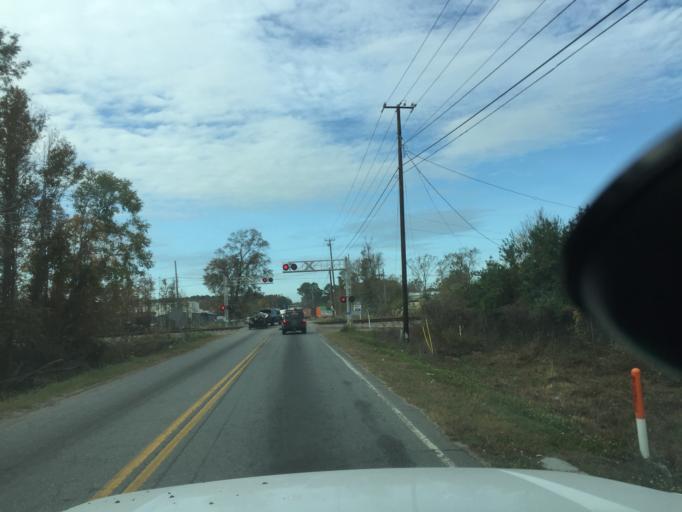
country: US
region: Georgia
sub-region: Chatham County
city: Garden City
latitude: 32.0796
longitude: -81.1453
